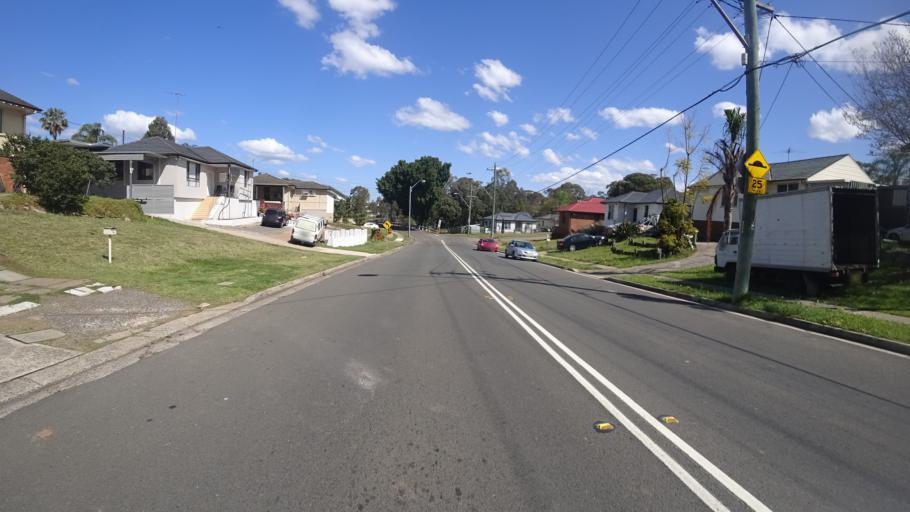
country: AU
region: New South Wales
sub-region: Fairfield
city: Cabramatta West
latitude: -33.9036
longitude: 150.9073
